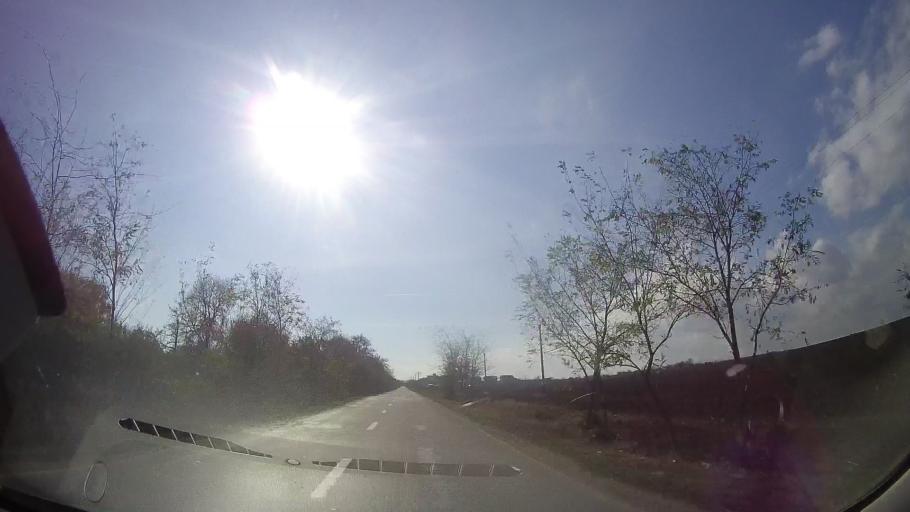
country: RO
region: Constanta
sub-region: Comuna Costinesti
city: Costinesti
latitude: 43.9607
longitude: 28.6361
